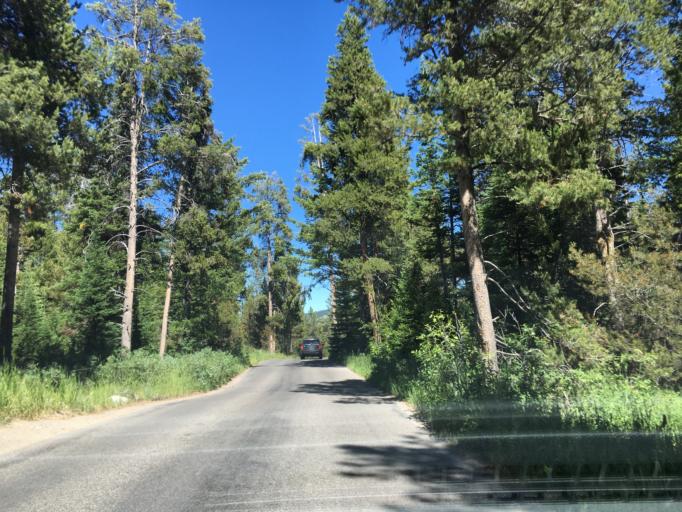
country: US
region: Wyoming
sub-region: Teton County
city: Moose Wilson Road
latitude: 43.6309
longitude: -110.7757
